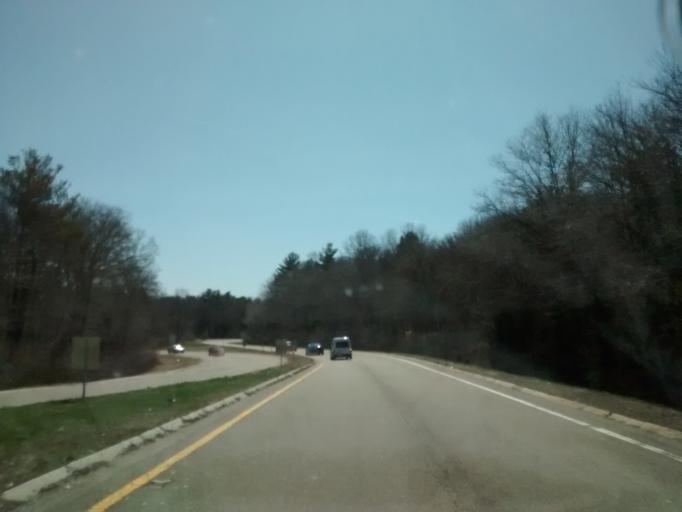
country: US
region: Massachusetts
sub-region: Norfolk County
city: Foxborough
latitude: 42.0270
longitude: -71.2608
